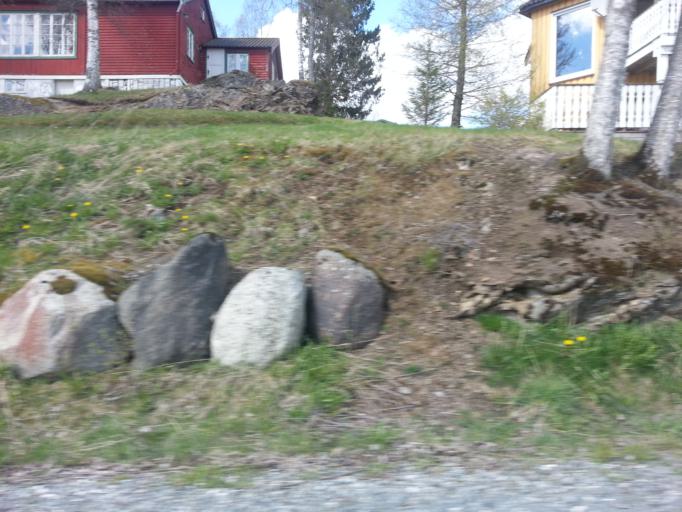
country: NO
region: Nord-Trondelag
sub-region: Levanger
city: Skogn
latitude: 63.6382
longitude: 11.2402
